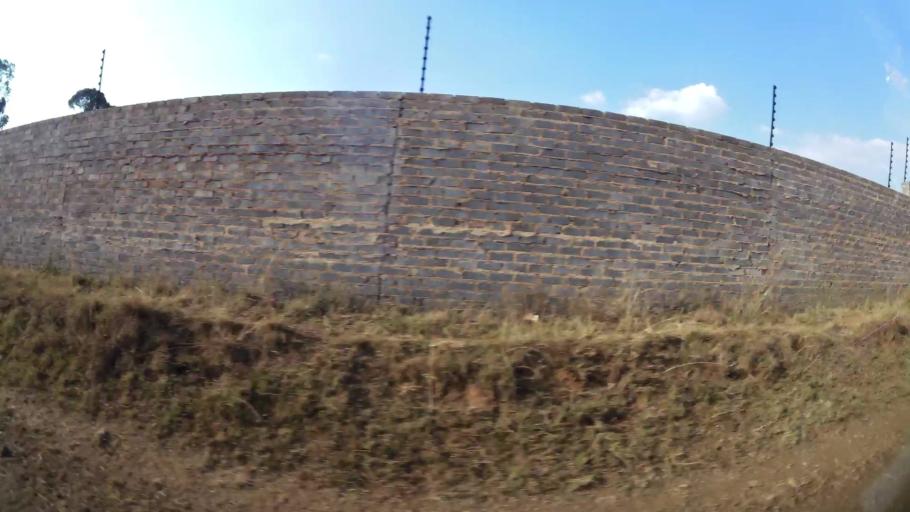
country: ZA
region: Gauteng
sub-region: Ekurhuleni Metropolitan Municipality
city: Benoni
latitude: -26.0999
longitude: 28.2899
